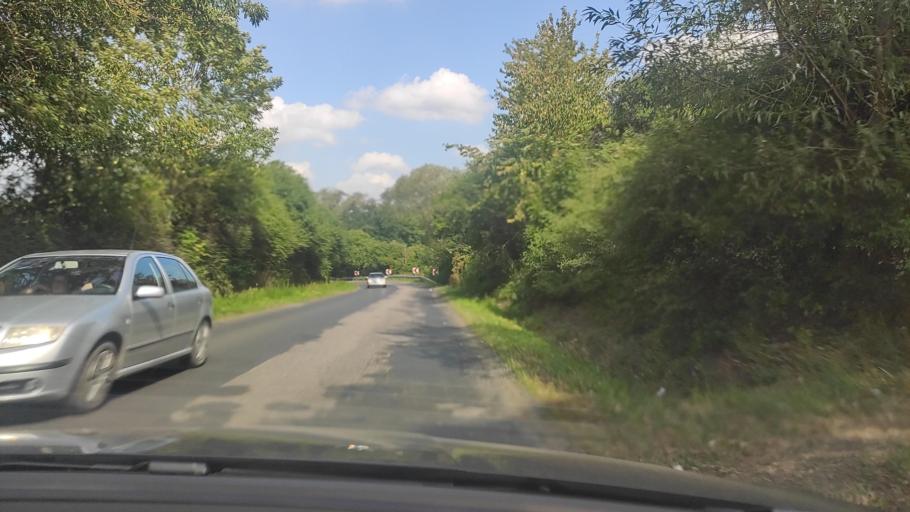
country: PL
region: Greater Poland Voivodeship
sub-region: Powiat poznanski
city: Kostrzyn
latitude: 52.4466
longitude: 17.1674
